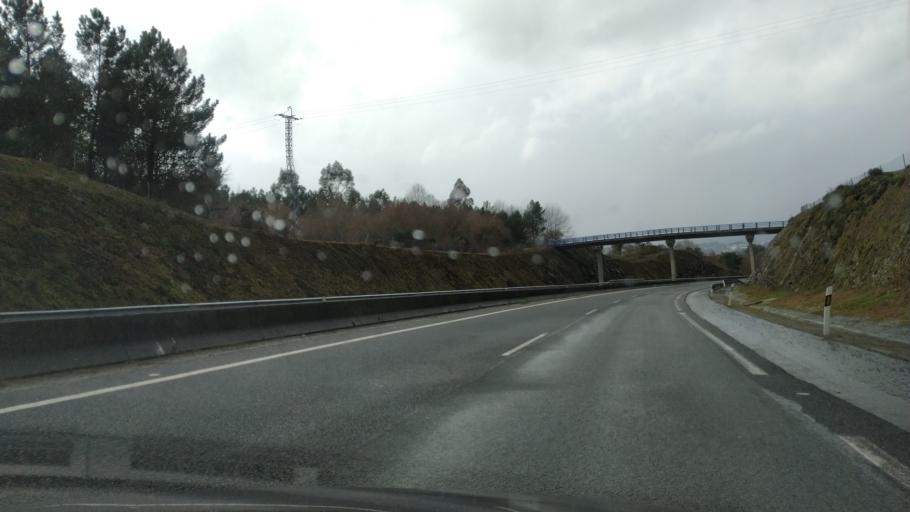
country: ES
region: Galicia
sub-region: Provincia de Pontevedra
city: Silleda
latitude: 42.7158
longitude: -8.2545
